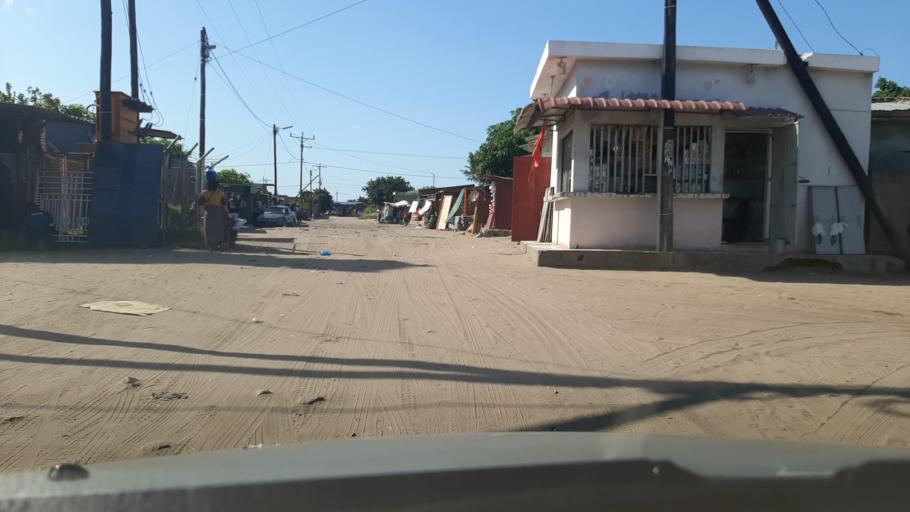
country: MZ
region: Maputo
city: Matola
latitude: -25.7916
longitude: 32.4879
